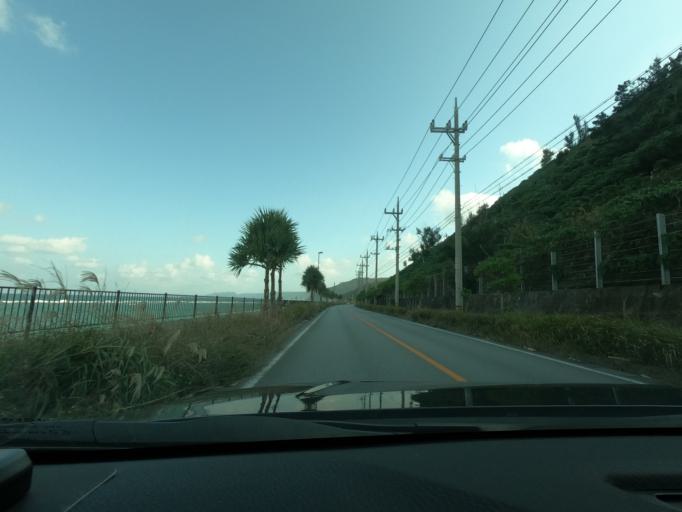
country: JP
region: Okinawa
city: Nago
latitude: 26.7621
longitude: 128.1915
